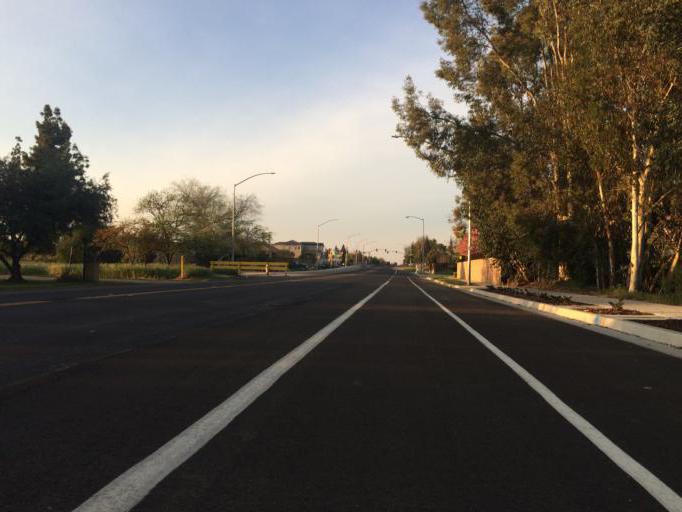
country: US
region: California
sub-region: Fresno County
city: Tarpey Village
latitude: 36.7986
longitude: -119.6730
